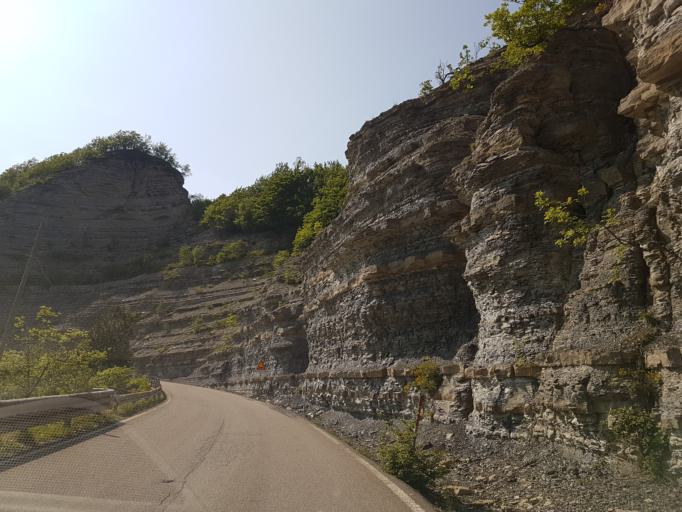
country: IT
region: Emilia-Romagna
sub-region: Forli-Cesena
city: San Piero in Bagno
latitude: 43.8110
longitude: 11.9341
